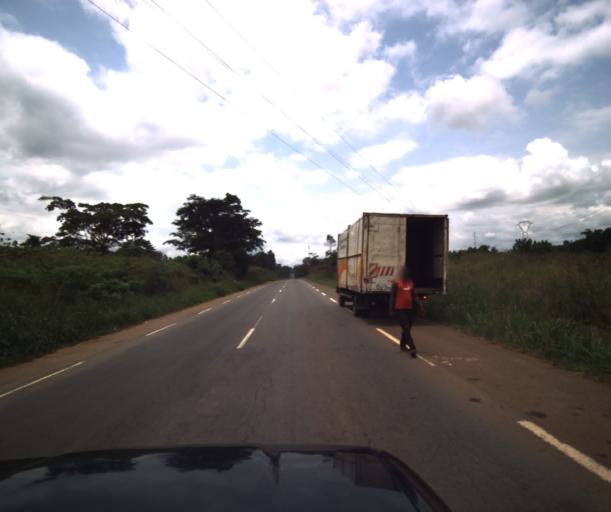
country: CM
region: Centre
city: Eseka
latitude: 3.8711
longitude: 10.9080
